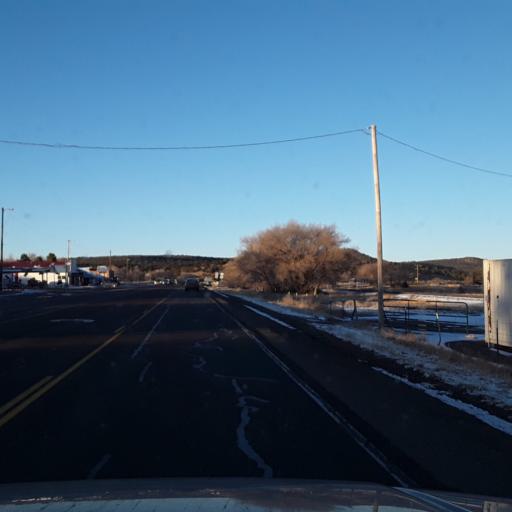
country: US
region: New Mexico
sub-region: Lincoln County
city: Carrizozo
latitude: 34.2495
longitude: -105.5947
